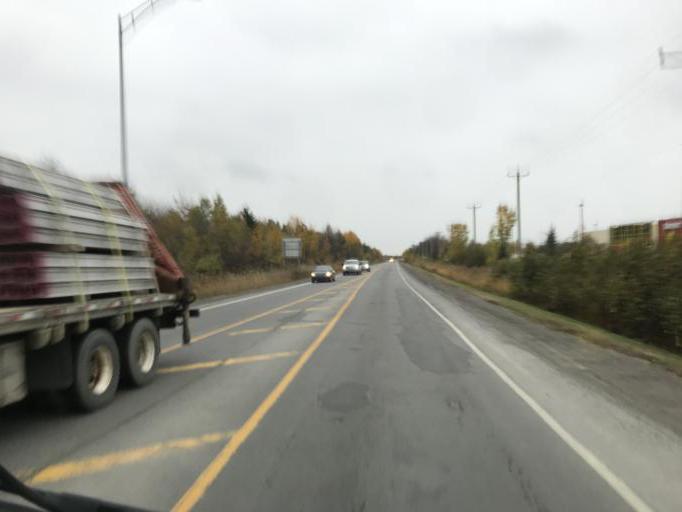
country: CA
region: Quebec
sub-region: Lanaudiere
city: Lorraine
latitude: 45.6890
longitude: -73.7803
